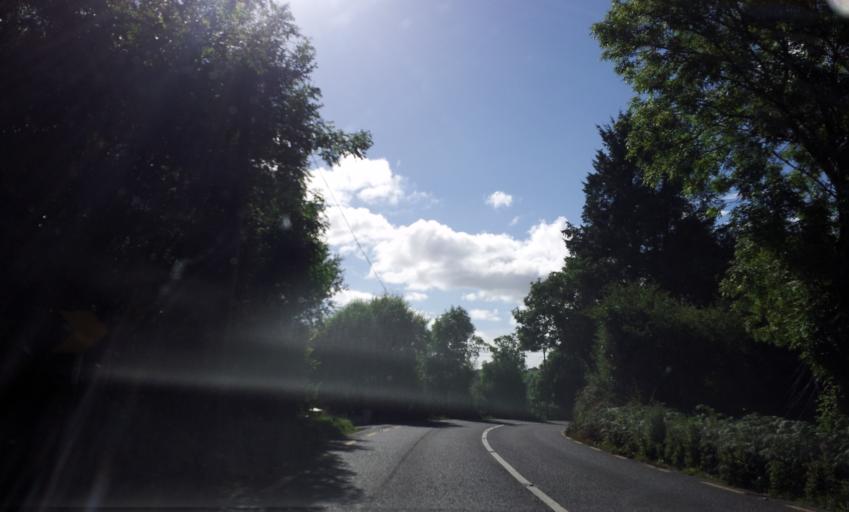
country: IE
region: Munster
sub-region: County Cork
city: Millstreet
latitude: 51.9241
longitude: -9.1152
